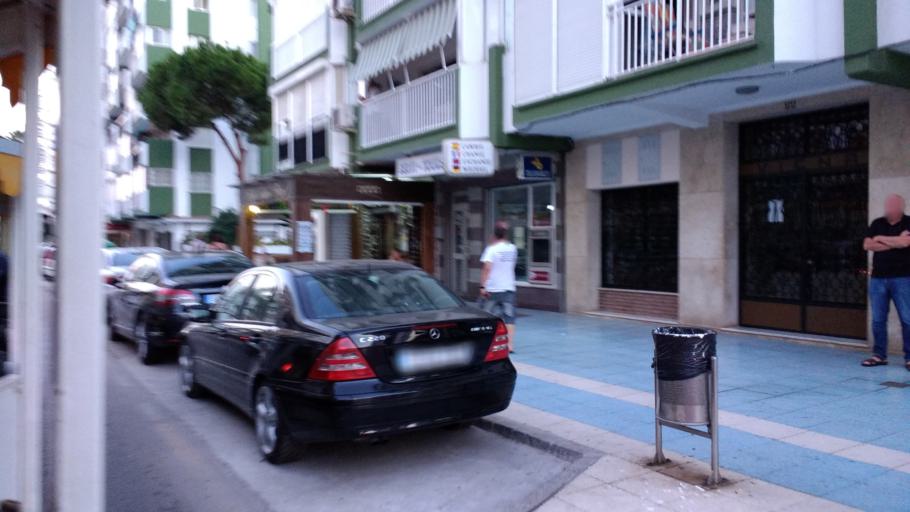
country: ES
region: Andalusia
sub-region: Provincia de Malaga
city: Velez-Malaga
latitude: 36.7370
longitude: -4.0980
